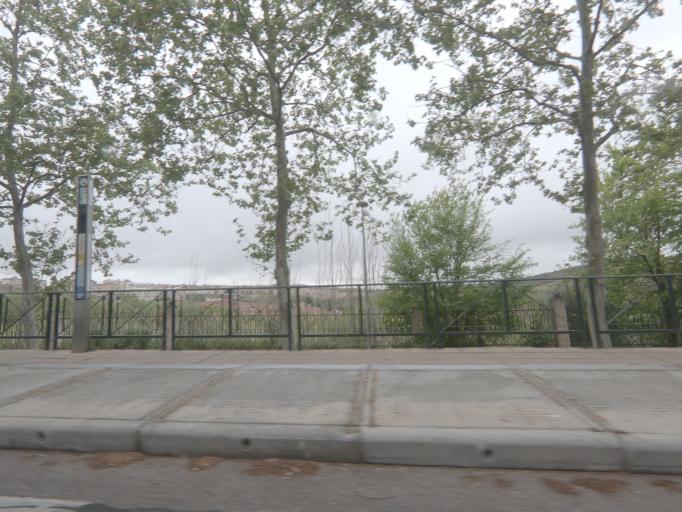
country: ES
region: Extremadura
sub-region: Provincia de Caceres
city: Caceres
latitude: 39.4765
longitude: -6.3796
